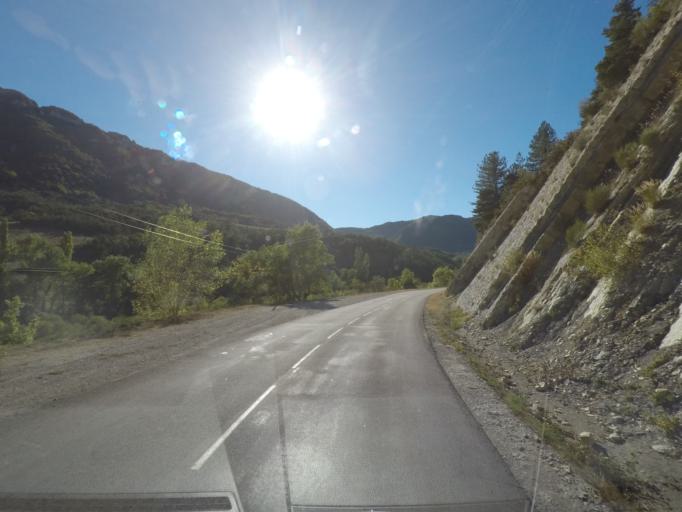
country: FR
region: Rhone-Alpes
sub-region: Departement de la Drome
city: Buis-les-Baronnies
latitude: 44.4661
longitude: 5.4391
